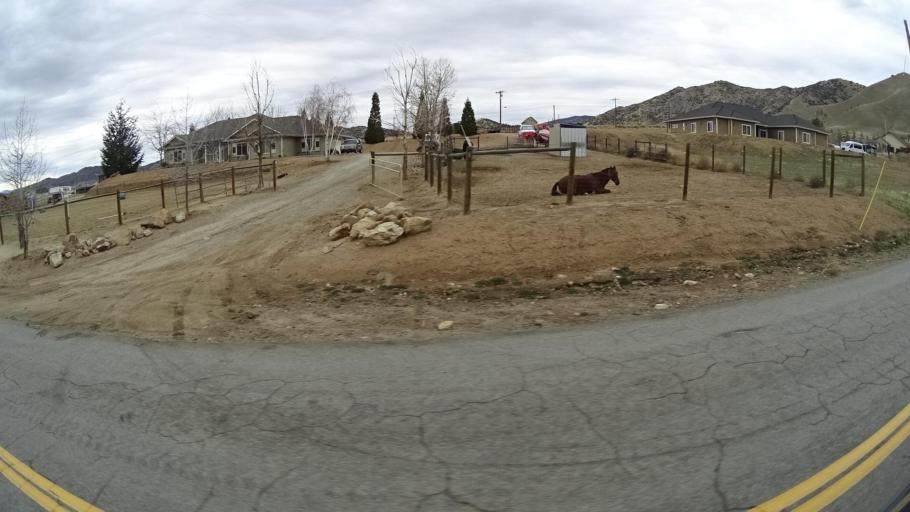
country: US
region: California
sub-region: Kern County
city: Bear Valley Springs
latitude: 35.1319
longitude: -118.5646
